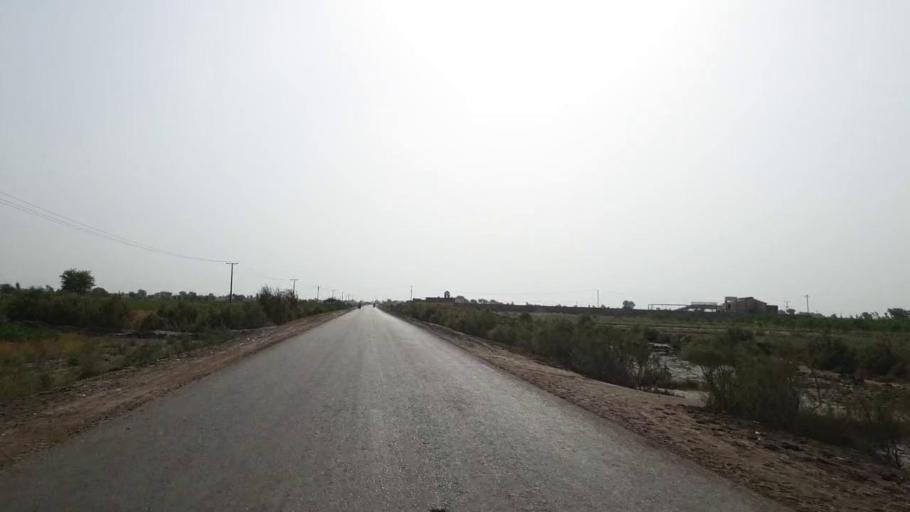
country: PK
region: Sindh
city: Jam Sahib
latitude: 26.2800
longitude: 68.5748
